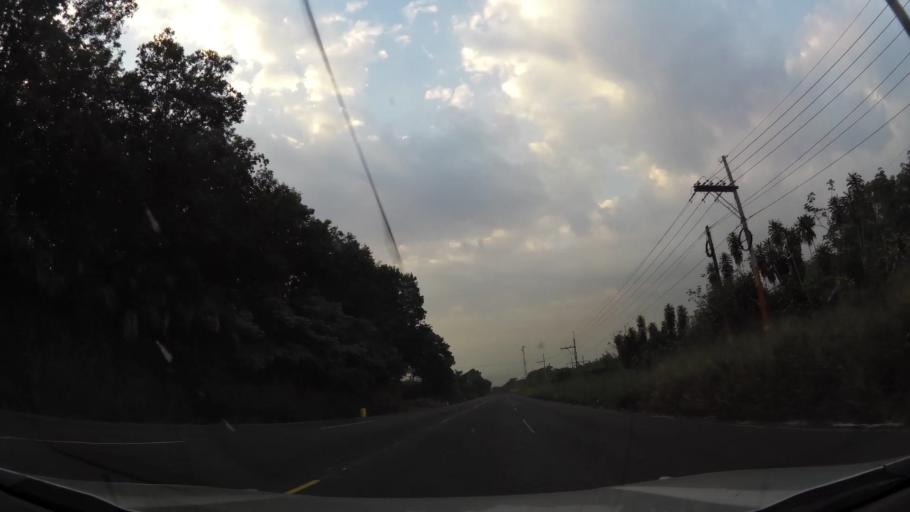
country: GT
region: Escuintla
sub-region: Municipio de La Democracia
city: La Democracia
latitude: 14.2721
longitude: -90.9063
